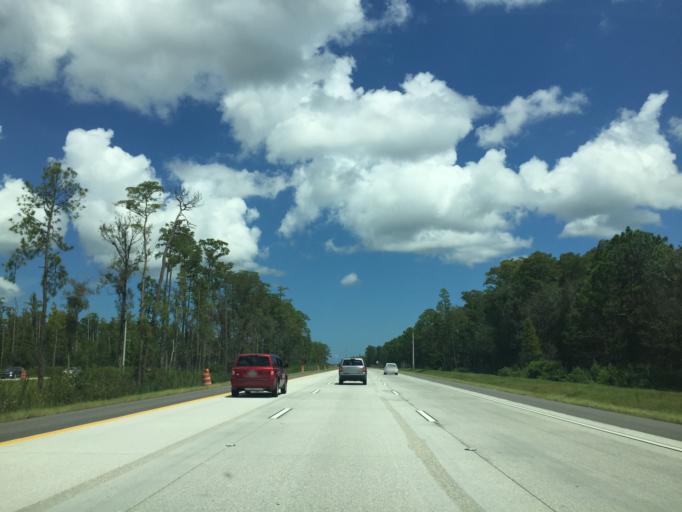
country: US
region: Florida
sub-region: Volusia County
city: Samsula-Spruce Creek
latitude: 29.0895
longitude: -81.1634
